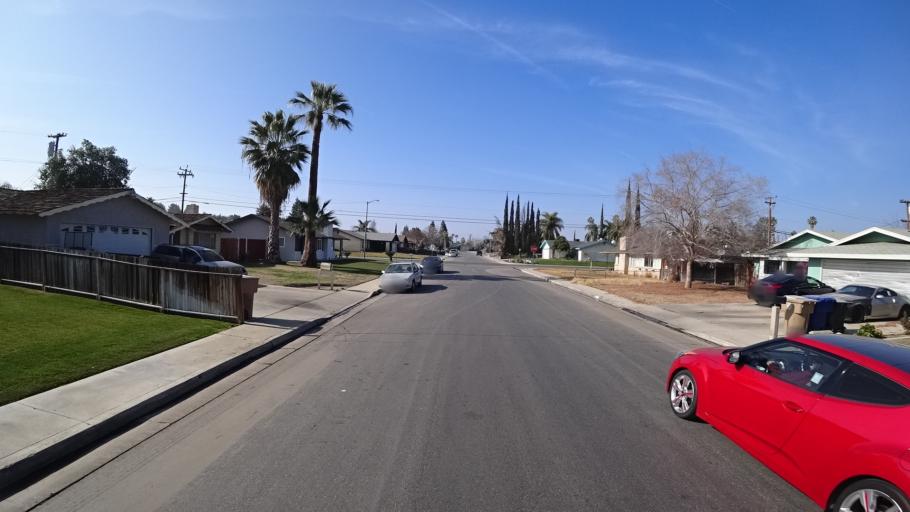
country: US
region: California
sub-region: Kern County
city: Bakersfield
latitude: 35.3267
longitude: -119.0428
